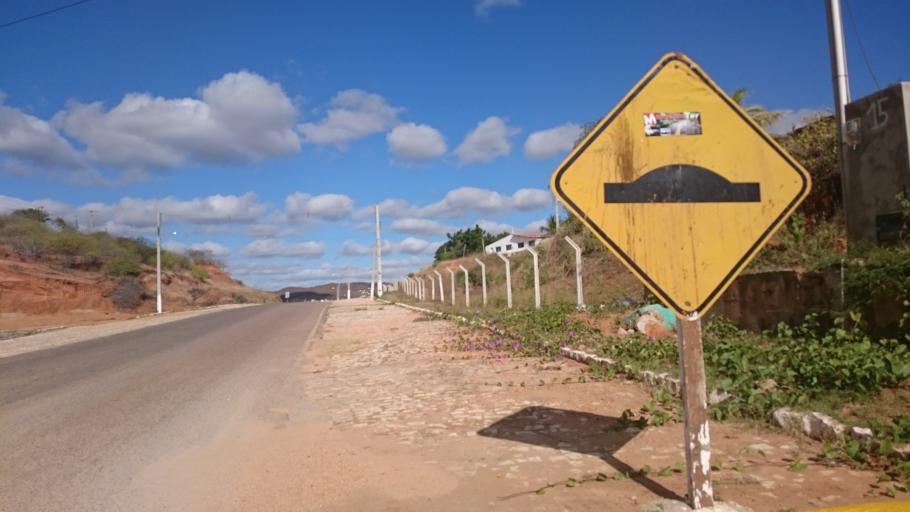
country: BR
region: Paraiba
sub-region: Catole Do Rocha
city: Sao Bento
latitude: -6.1529
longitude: -37.7605
